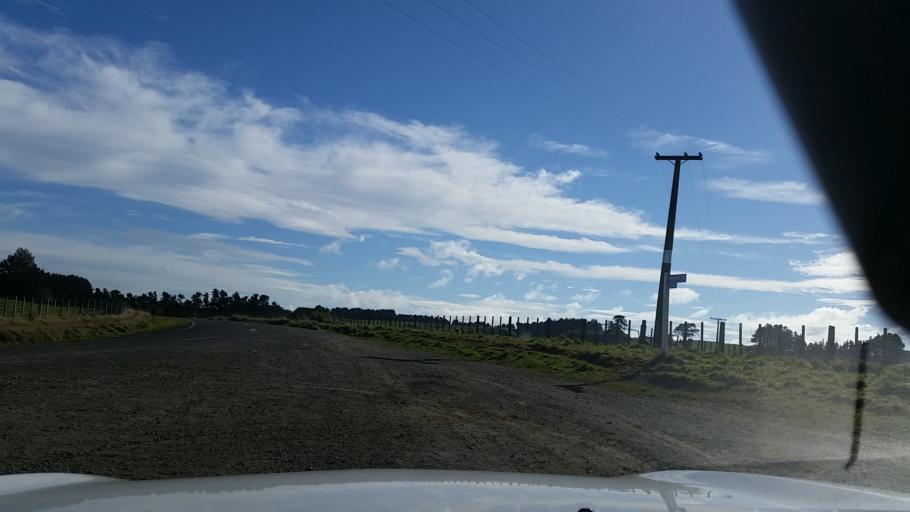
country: NZ
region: Taranaki
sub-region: South Taranaki District
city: Patea
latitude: -39.6997
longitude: 174.6307
